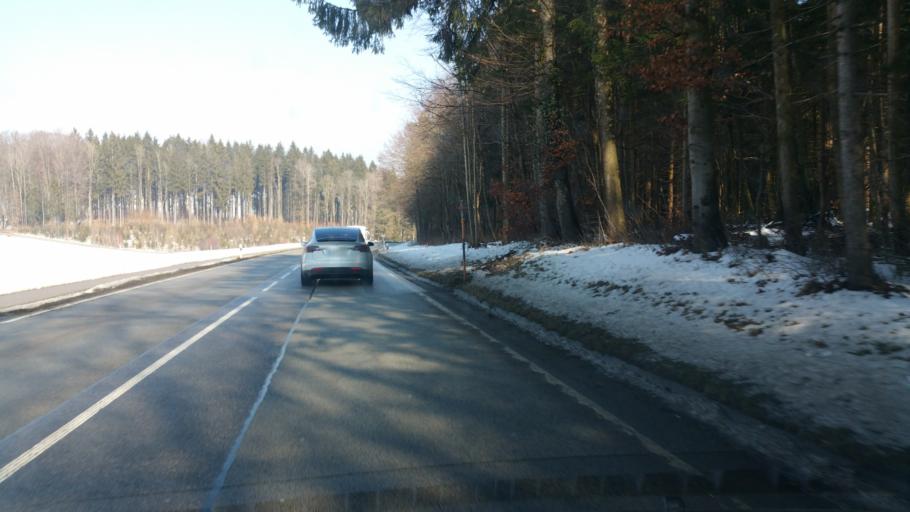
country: DE
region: Bavaria
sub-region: Upper Bavaria
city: Miesbach
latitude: 47.8030
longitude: 11.8546
